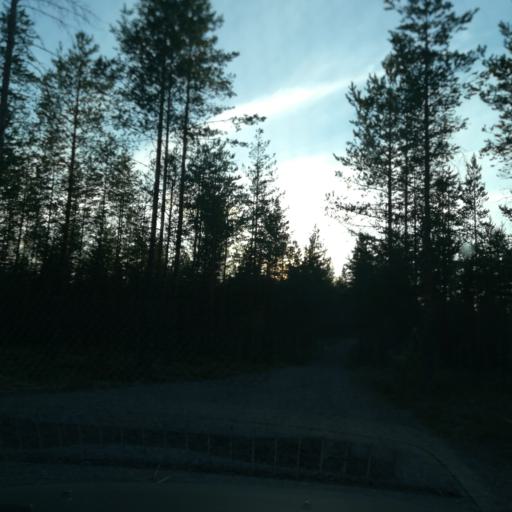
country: FI
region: Southern Savonia
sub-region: Mikkeli
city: Puumala
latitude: 61.4333
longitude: 28.4641
